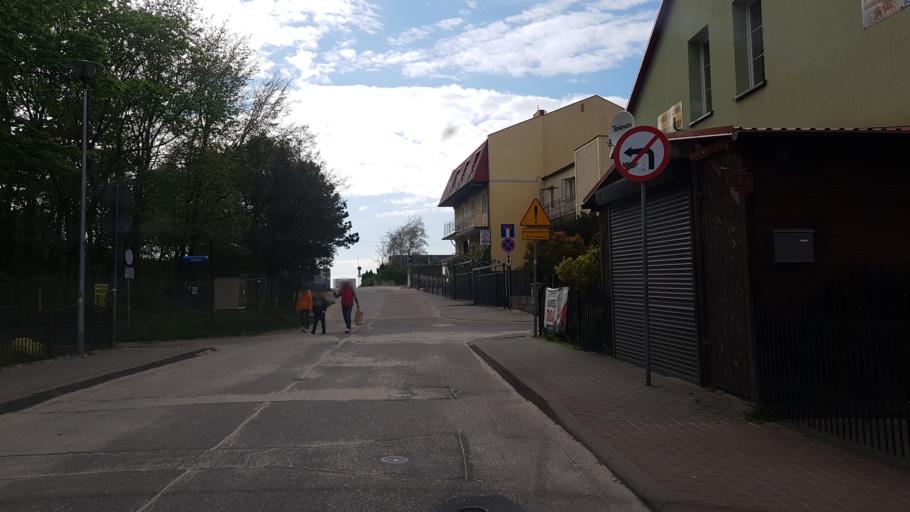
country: PL
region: West Pomeranian Voivodeship
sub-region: Powiat slawienski
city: Darlowo
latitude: 54.4379
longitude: 16.3770
